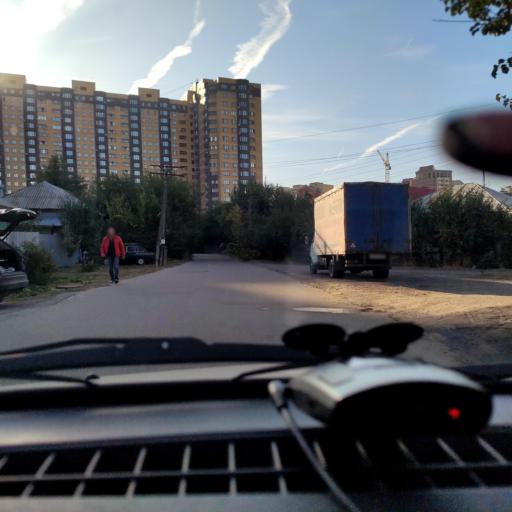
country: RU
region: Voronezj
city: Voronezh
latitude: 51.6747
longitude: 39.1629
